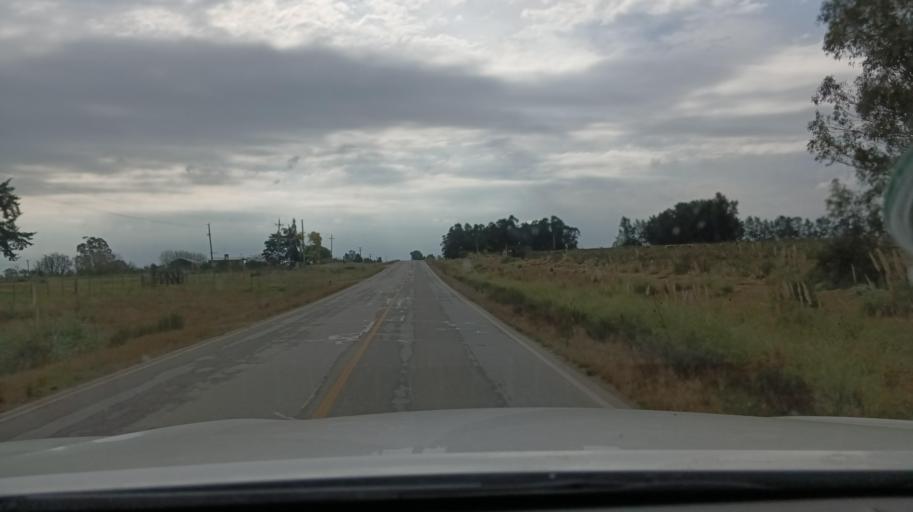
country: UY
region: Canelones
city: Sauce
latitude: -34.6406
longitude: -56.1071
